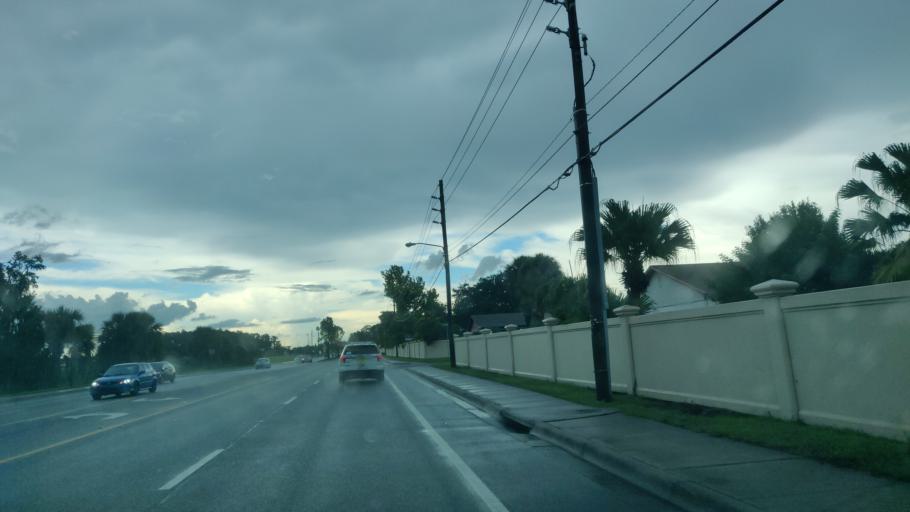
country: US
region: Florida
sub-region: Osceola County
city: Kissimmee
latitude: 28.3170
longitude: -81.4243
